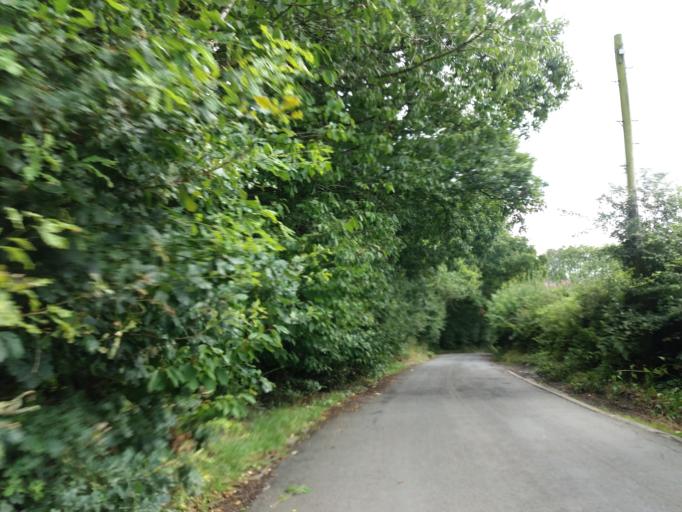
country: GB
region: England
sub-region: Lancashire
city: Euxton
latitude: 53.6651
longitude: -2.6652
